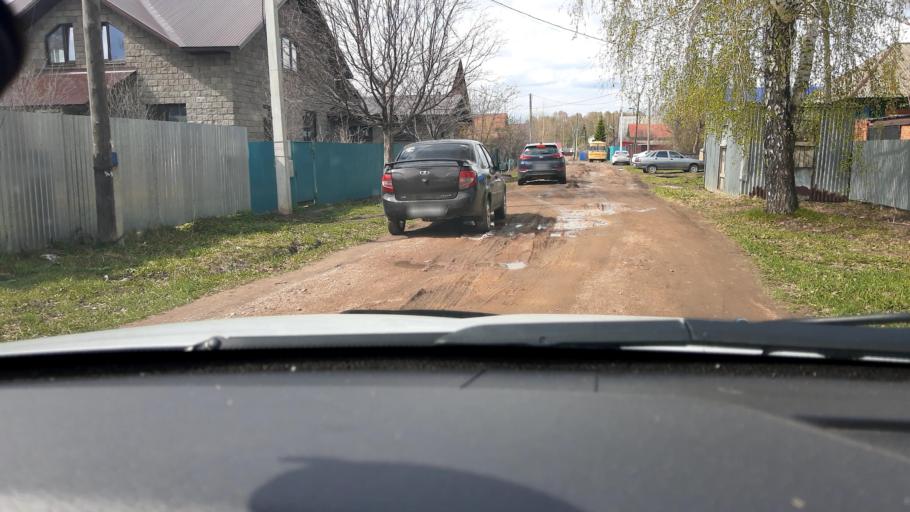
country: RU
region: Bashkortostan
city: Iglino
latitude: 54.8289
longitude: 56.4034
